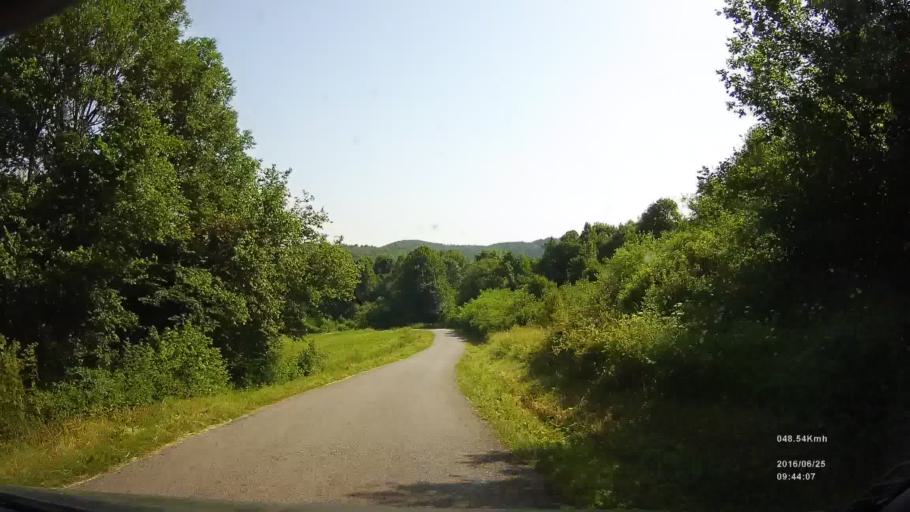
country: SK
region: Banskobystricky
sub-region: Okres Banska Bystrica
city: Banska Bystrica
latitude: 48.7058
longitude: 19.2279
